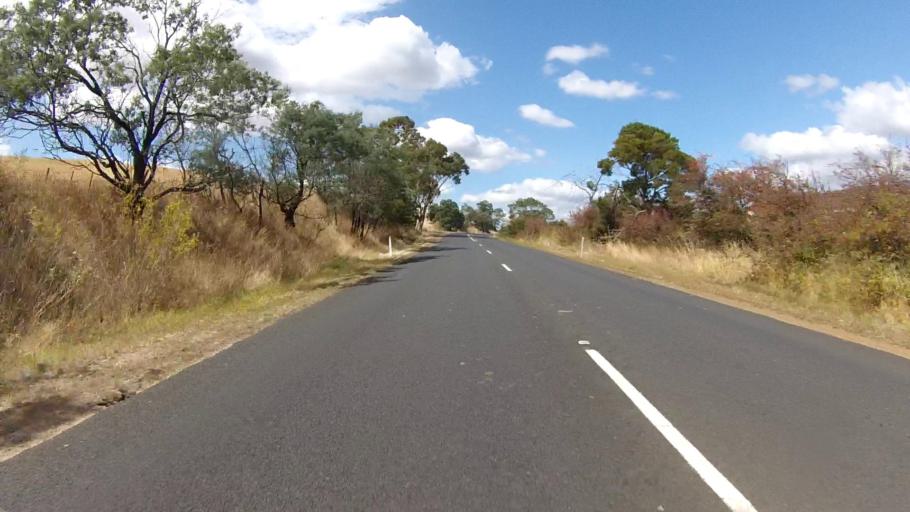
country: AU
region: Tasmania
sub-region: Derwent Valley
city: New Norfolk
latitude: -42.7345
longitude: 146.9274
